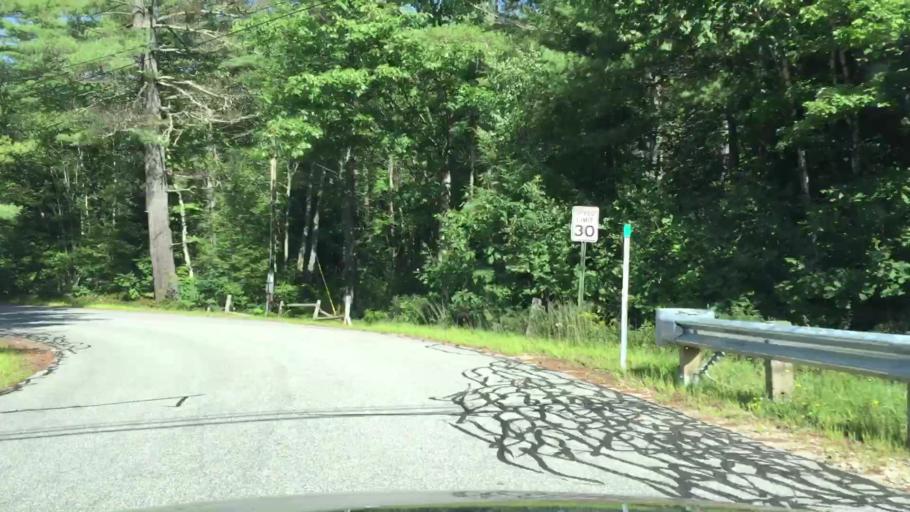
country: US
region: New Hampshire
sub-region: Grafton County
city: Ashland
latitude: 43.7183
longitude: -71.6235
